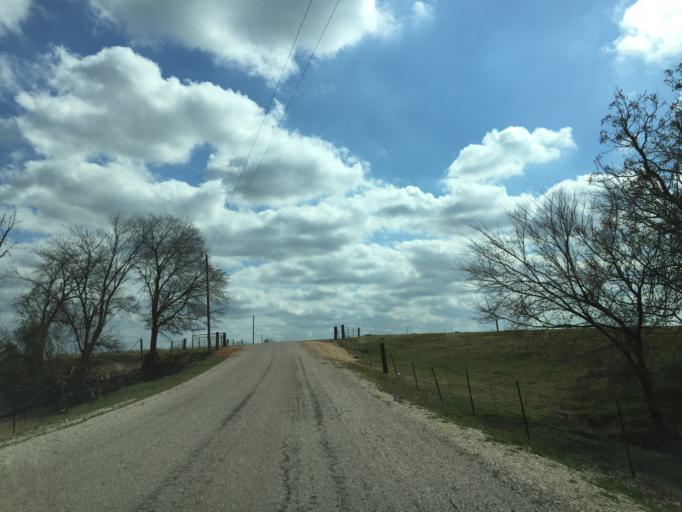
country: US
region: Texas
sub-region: Williamson County
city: Granger
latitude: 30.7093
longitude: -97.4723
